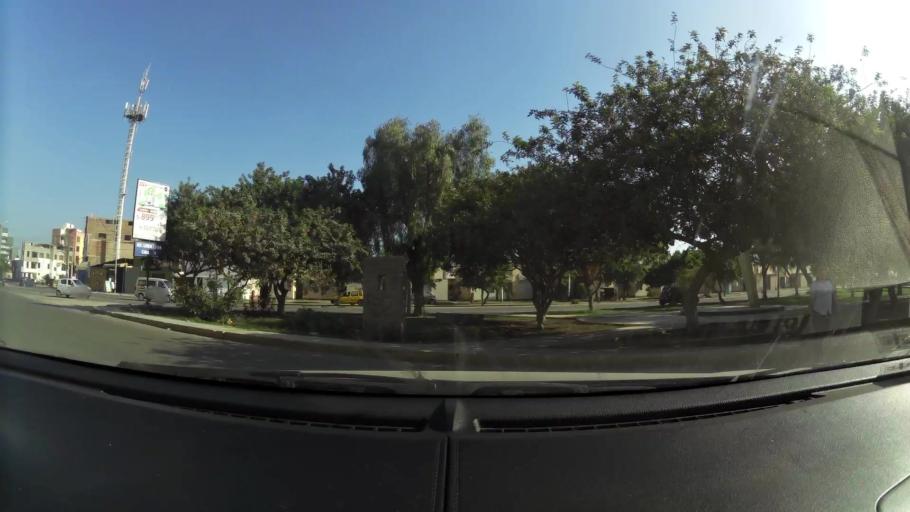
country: PE
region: Lambayeque
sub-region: Provincia de Chiclayo
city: Chiclayo
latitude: -6.7656
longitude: -79.8496
